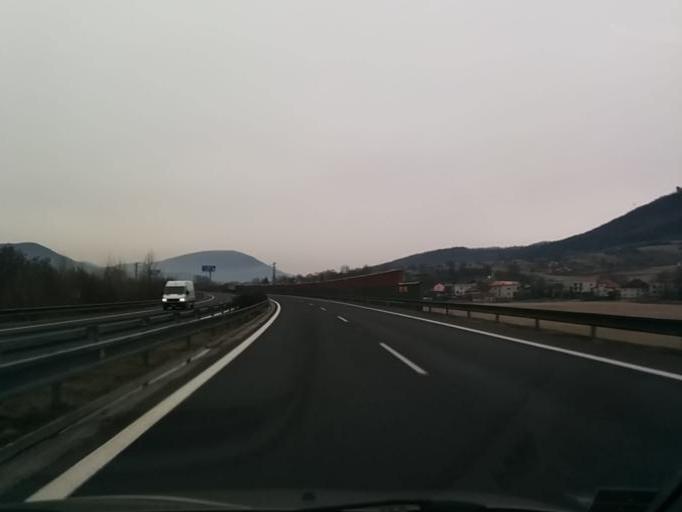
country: SK
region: Banskobystricky
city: Nova Bana
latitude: 48.3751
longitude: 18.6069
